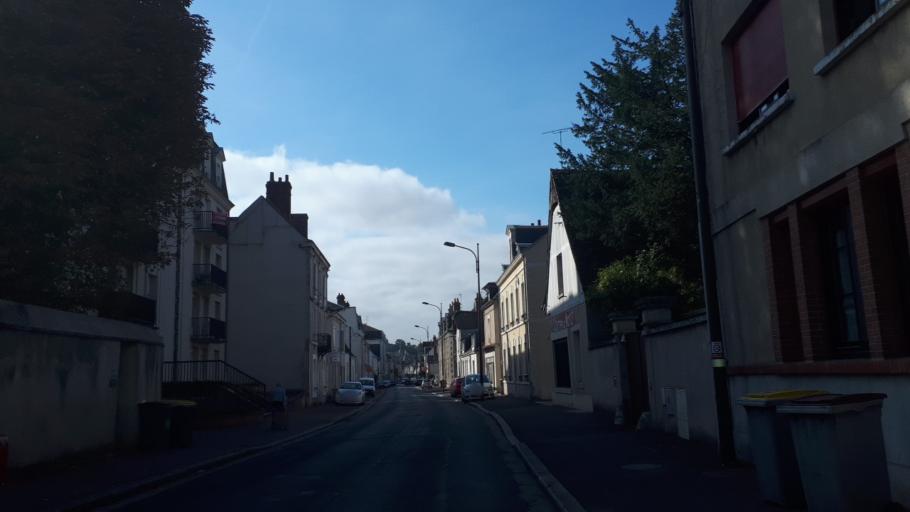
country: FR
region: Centre
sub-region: Departement du Loir-et-Cher
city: Vendome
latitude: 47.8009
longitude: 1.0696
